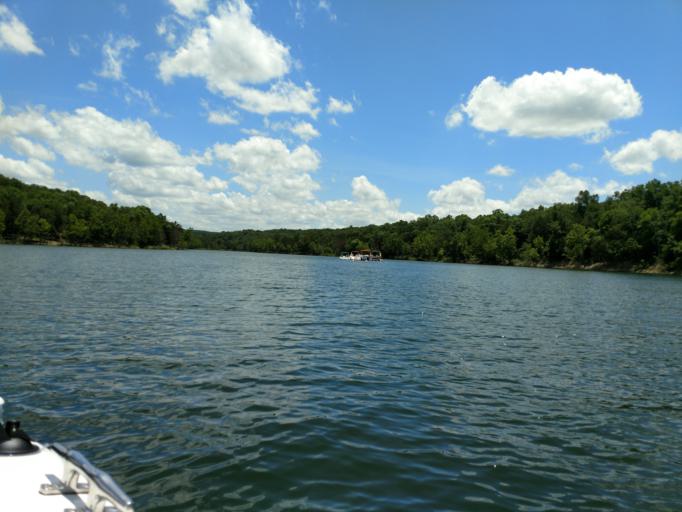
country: US
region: Missouri
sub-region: Barry County
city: Shell Knob
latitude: 36.5717
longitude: -93.5630
